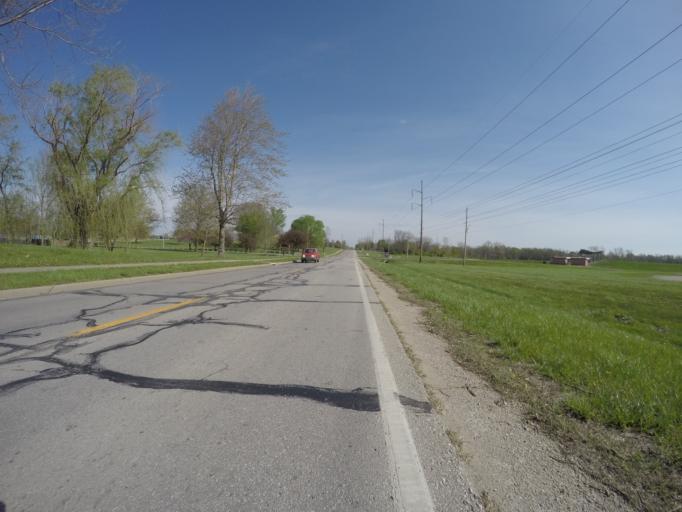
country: US
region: Missouri
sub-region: Jackson County
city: Grandview
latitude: 38.8753
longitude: -94.5082
